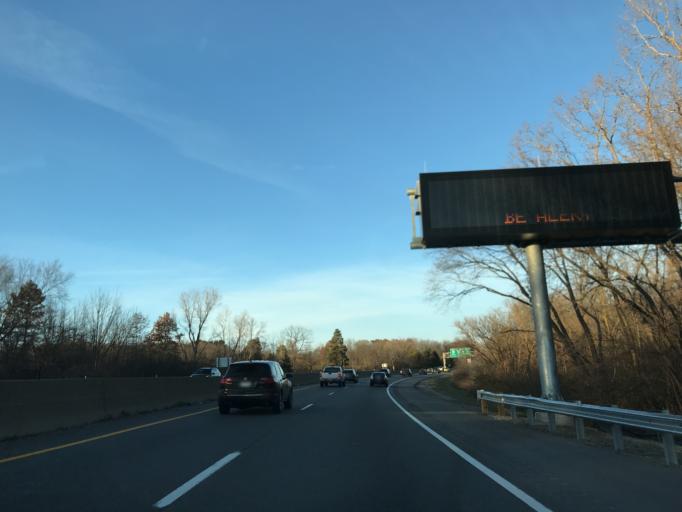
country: US
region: Michigan
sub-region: Washtenaw County
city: Ann Arbor
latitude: 42.3082
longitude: -83.7435
